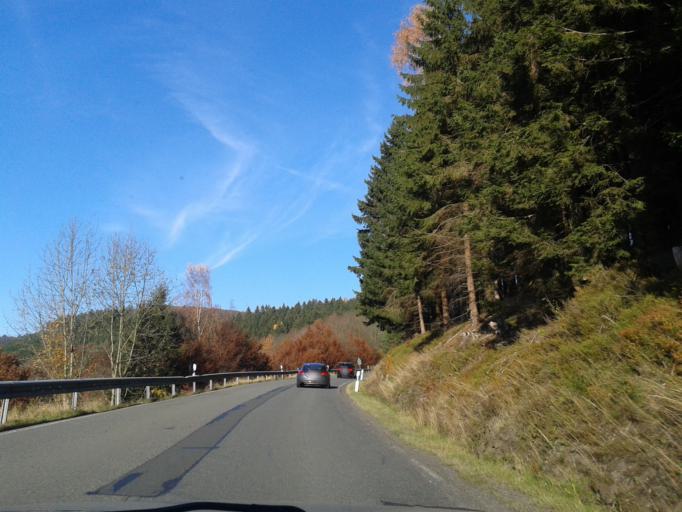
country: DE
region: North Rhine-Westphalia
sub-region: Regierungsbezirk Arnsberg
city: Bad Berleburg
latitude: 51.1144
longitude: 8.4311
